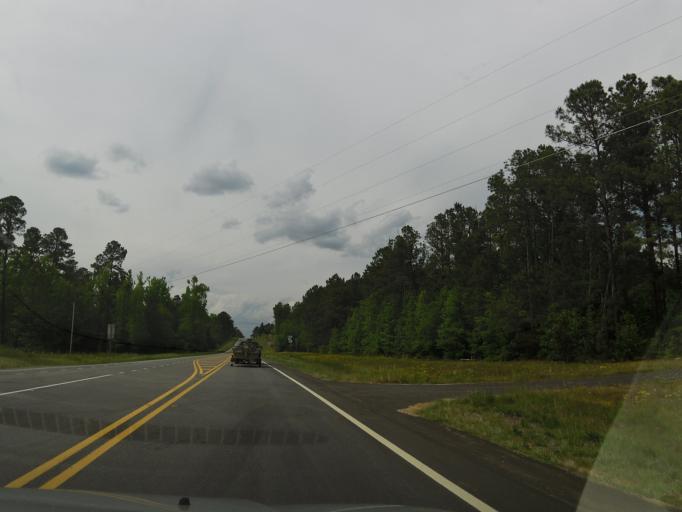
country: US
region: Georgia
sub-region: McDuffie County
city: Thomson
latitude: 33.4355
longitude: -82.4896
